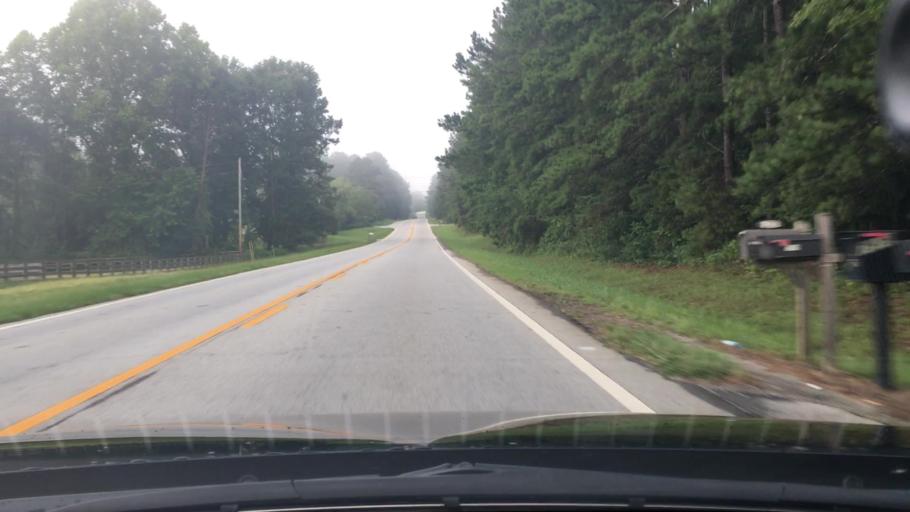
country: US
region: Georgia
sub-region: Fayette County
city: Peachtree City
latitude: 33.3754
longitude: -84.6271
